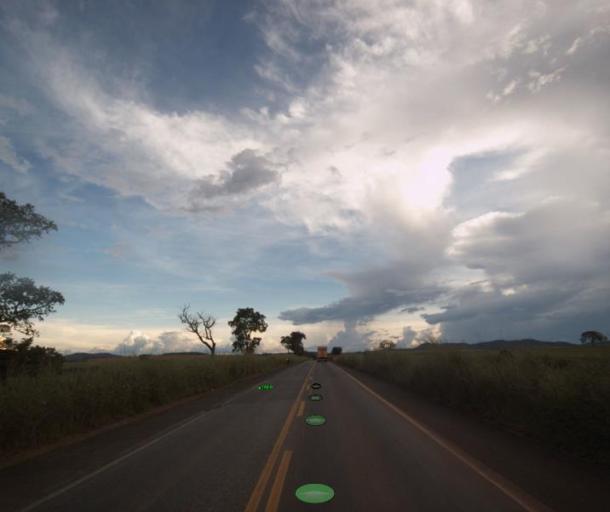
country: BR
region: Goias
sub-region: Uruacu
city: Uruacu
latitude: -14.1192
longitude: -49.1069
